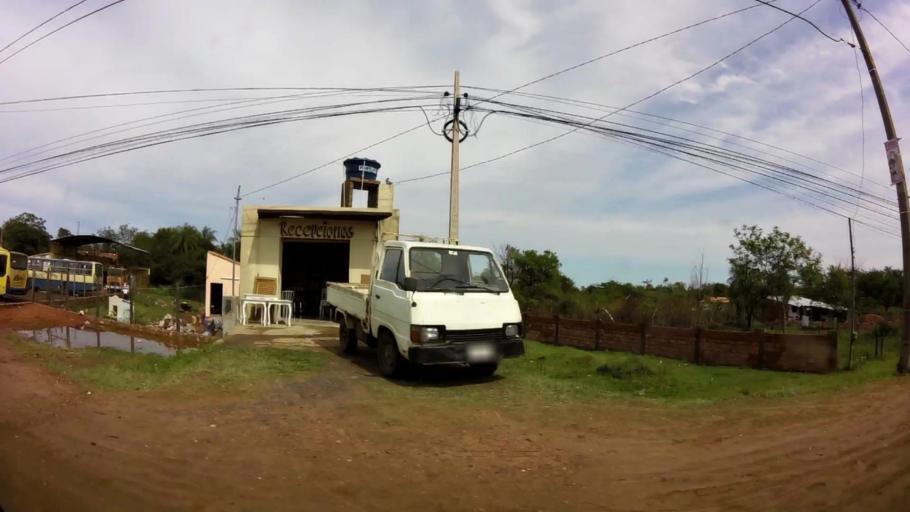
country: PY
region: Central
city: Limpio
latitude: -25.1582
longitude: -57.4744
